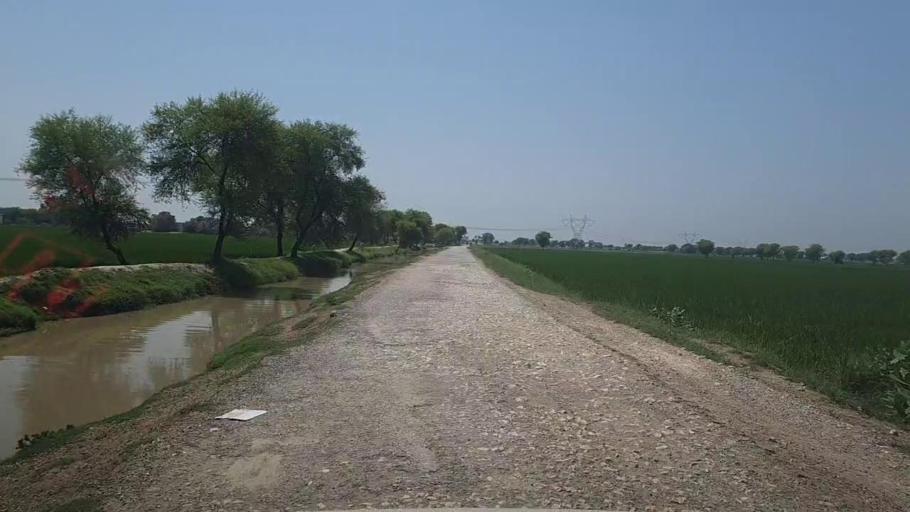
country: PK
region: Sindh
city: Kandhkot
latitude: 28.3272
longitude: 69.3851
